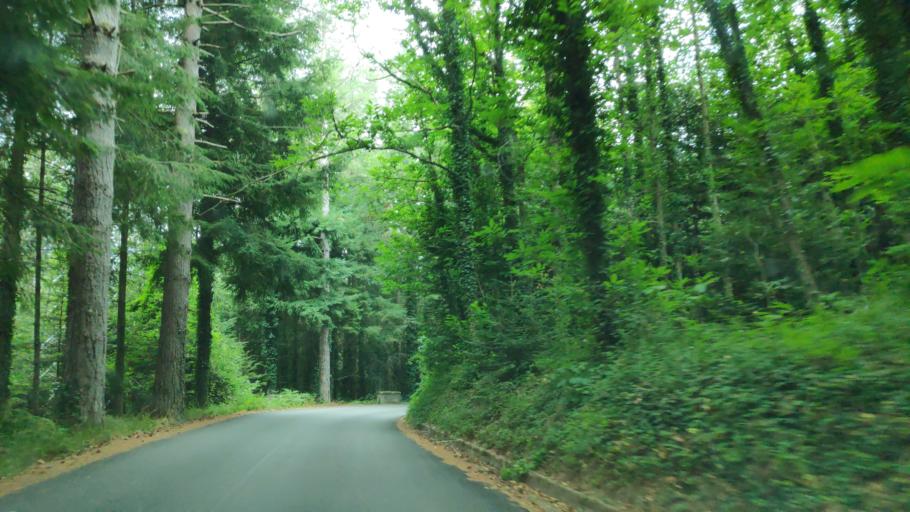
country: IT
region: Calabria
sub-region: Provincia di Vibo-Valentia
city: Mongiana
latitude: 38.5155
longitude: 16.3121
